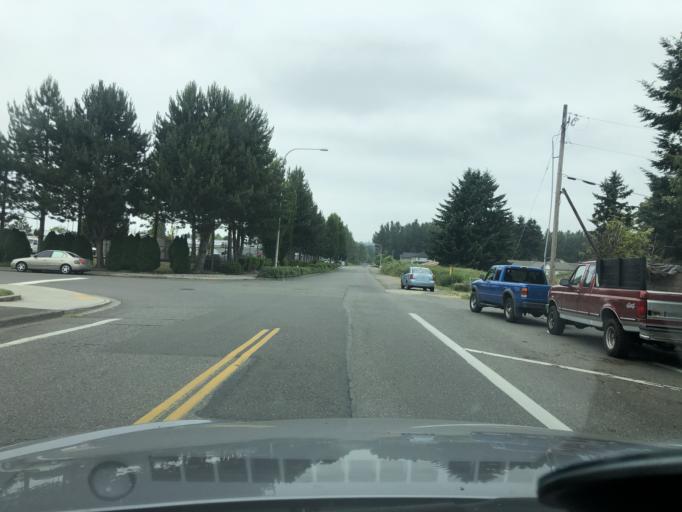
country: US
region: Washington
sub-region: King County
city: Auburn
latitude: 47.3424
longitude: -122.2194
